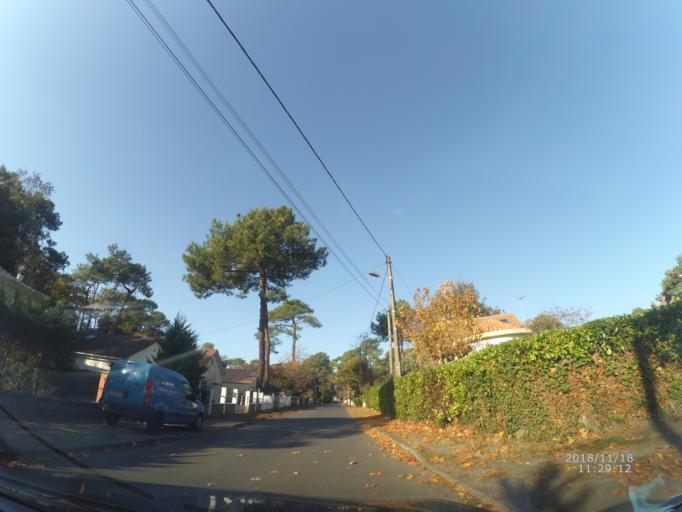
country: FR
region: Pays de la Loire
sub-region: Departement de la Loire-Atlantique
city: Saint-Michel-Chef-Chef
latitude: 47.2157
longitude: -2.1537
